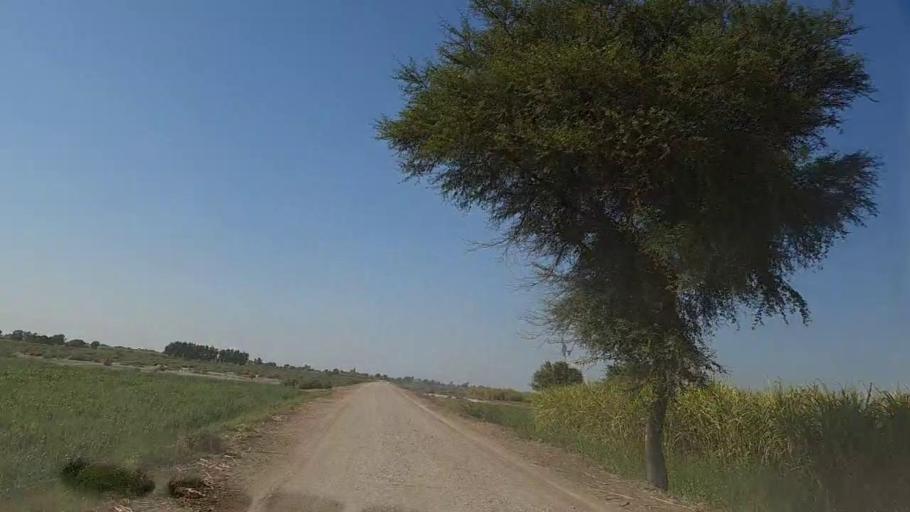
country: PK
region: Sindh
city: Digri
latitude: 25.1848
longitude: 69.0035
